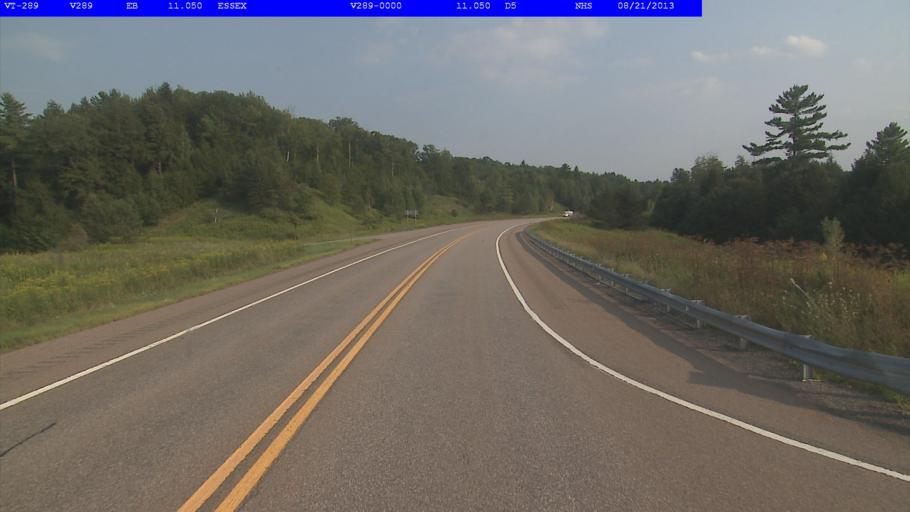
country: US
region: Vermont
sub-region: Chittenden County
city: Essex Junction
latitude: 44.4929
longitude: -73.0654
